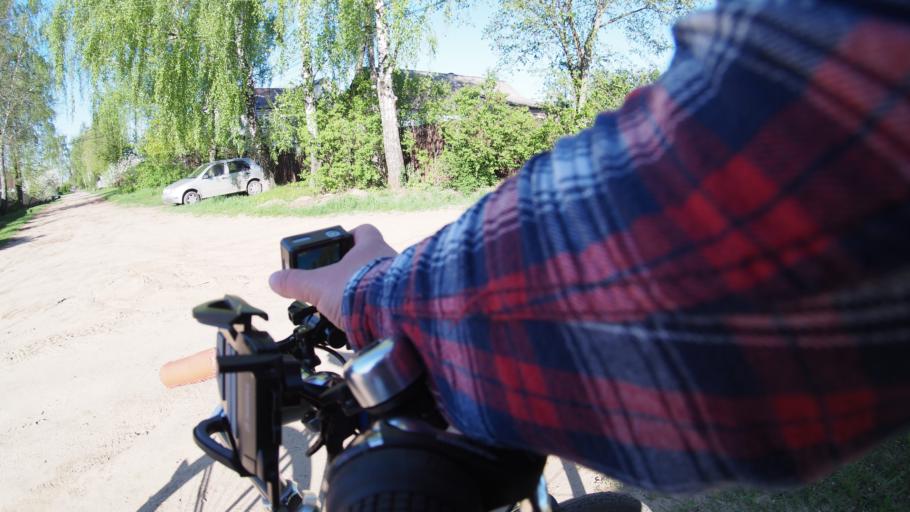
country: RU
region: Moskovskaya
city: Ramenskoye
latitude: 55.5518
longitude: 38.1897
